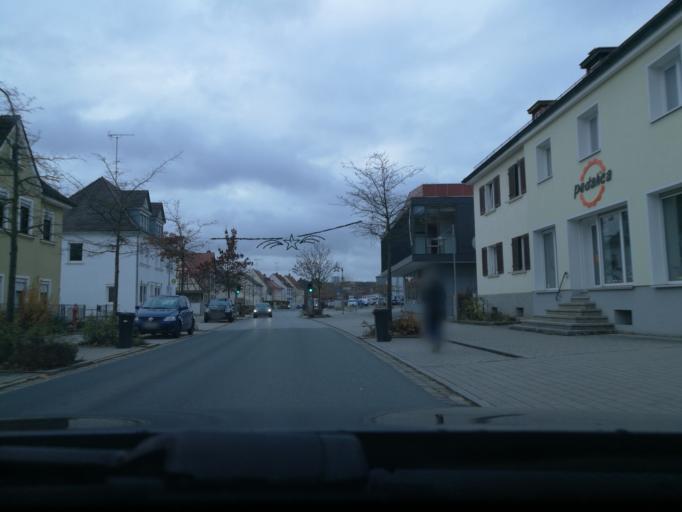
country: DE
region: Bavaria
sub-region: Regierungsbezirk Mittelfranken
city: Heroldsberg
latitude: 49.5292
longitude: 11.1510
